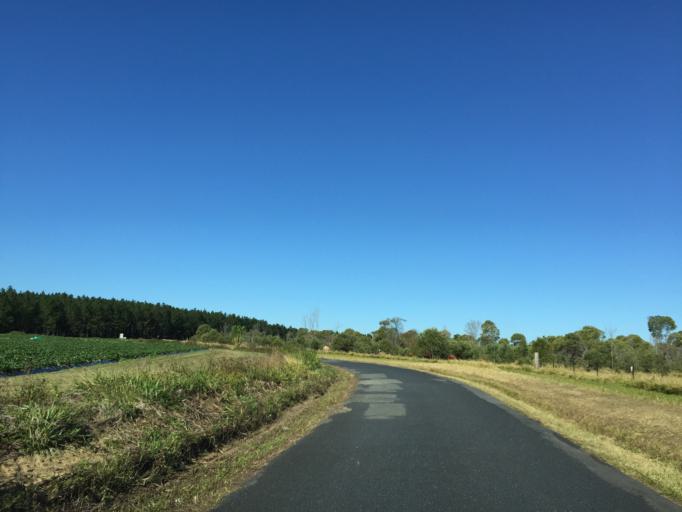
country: AU
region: Queensland
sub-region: Moreton Bay
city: Caboolture
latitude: -27.0230
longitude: 152.9856
